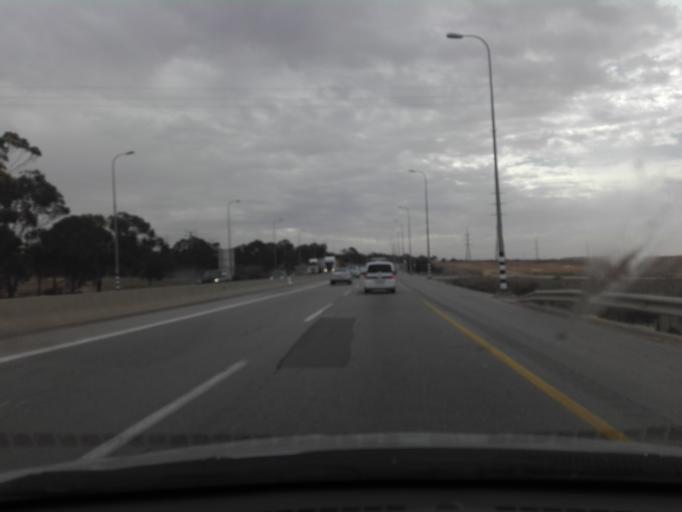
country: IL
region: Southern District
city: Lehavim
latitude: 31.3674
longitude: 34.7951
